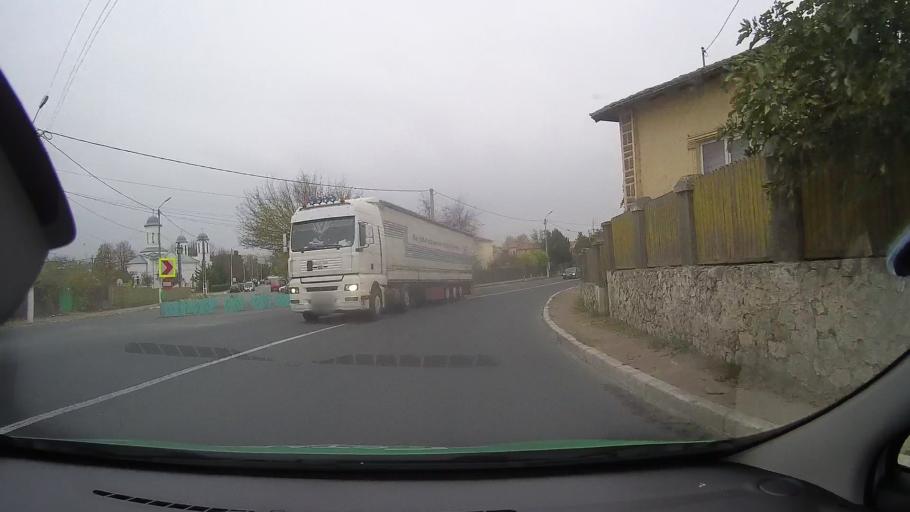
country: RO
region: Constanta
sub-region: Oras Harsova
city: Harsova
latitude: 44.6874
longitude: 27.9545
